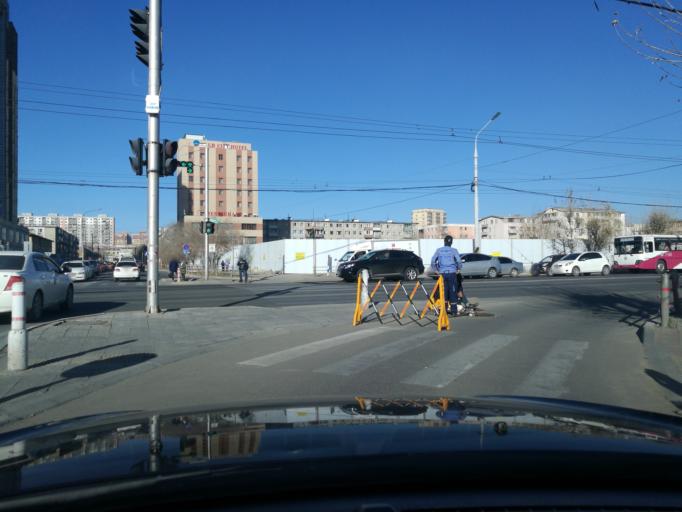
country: MN
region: Ulaanbaatar
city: Ulaanbaatar
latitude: 47.8988
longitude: 106.9018
